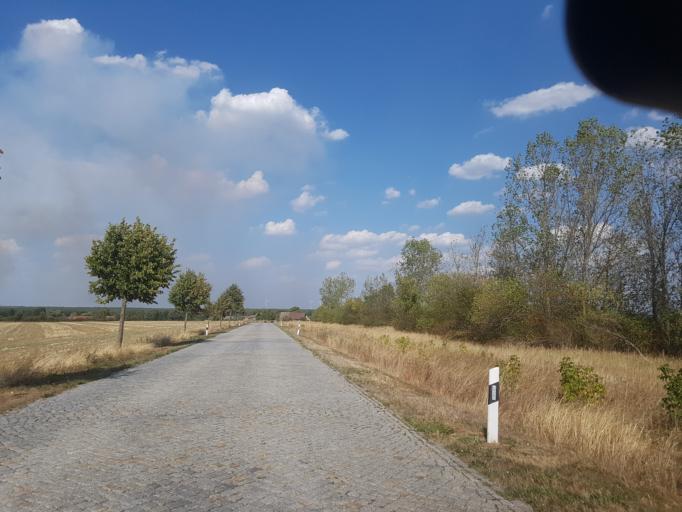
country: DE
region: Brandenburg
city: Niedergorsdorf
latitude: 52.0071
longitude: 12.9181
